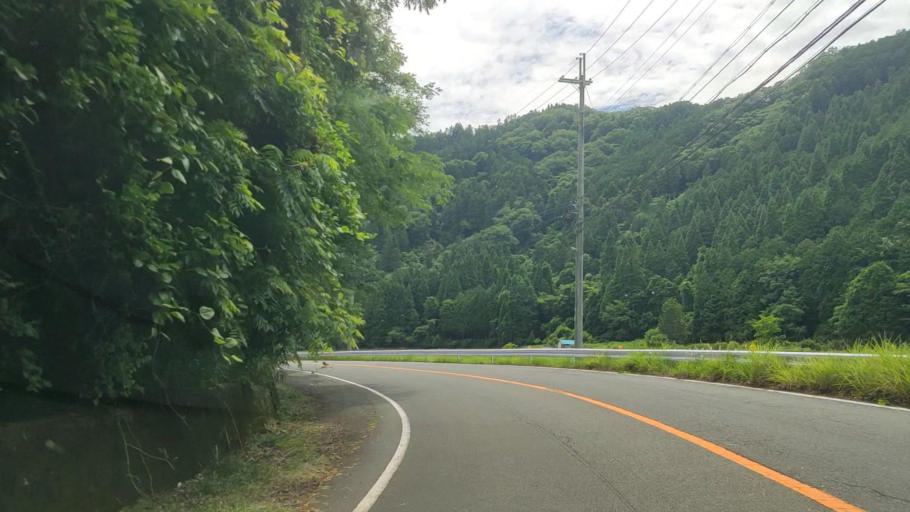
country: JP
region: Hyogo
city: Yamazakicho-nakabirose
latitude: 35.0738
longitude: 134.3571
